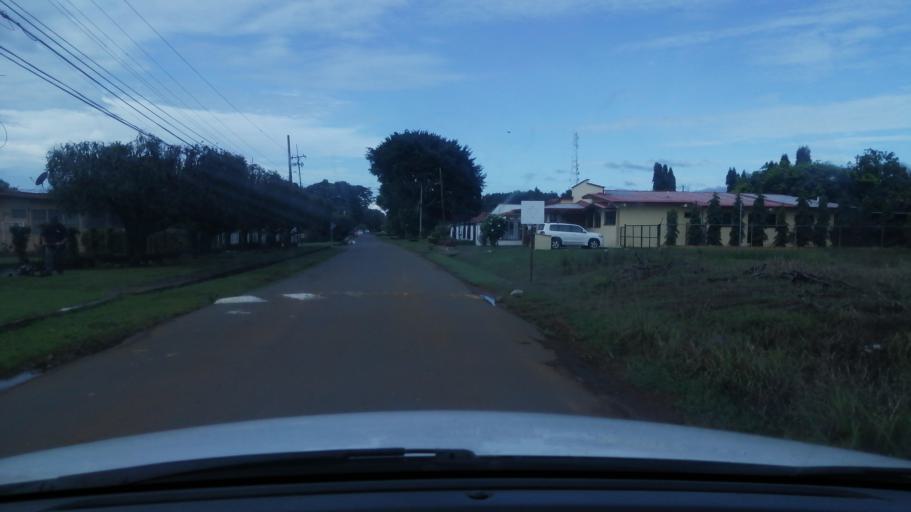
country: PA
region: Chiriqui
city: El Quiteno
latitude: 8.4595
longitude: -82.4180
